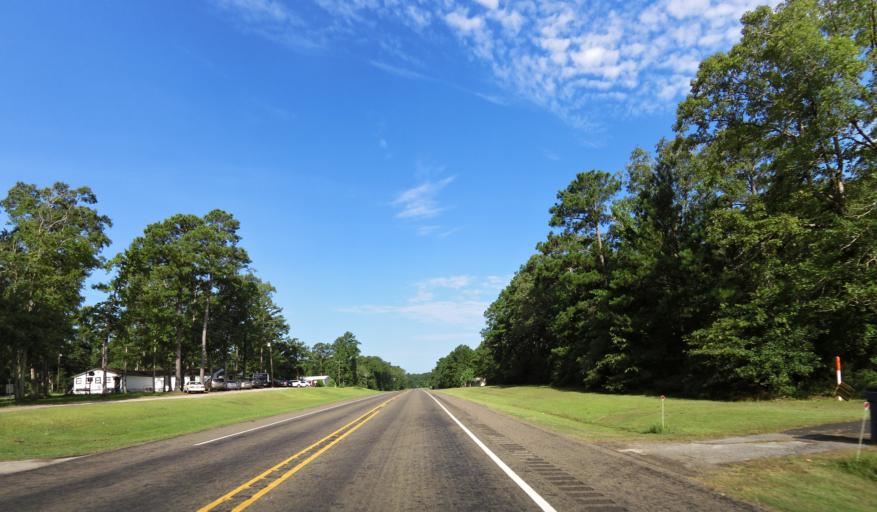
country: US
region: Texas
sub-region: Angelina County
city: Huntington
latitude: 31.1838
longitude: -94.3628
